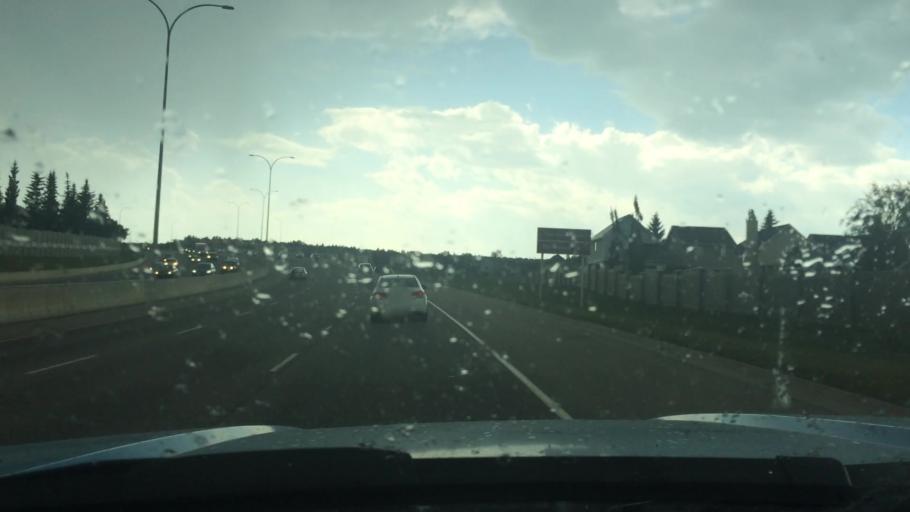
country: CA
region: Alberta
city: Calgary
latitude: 51.1444
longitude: -114.1163
